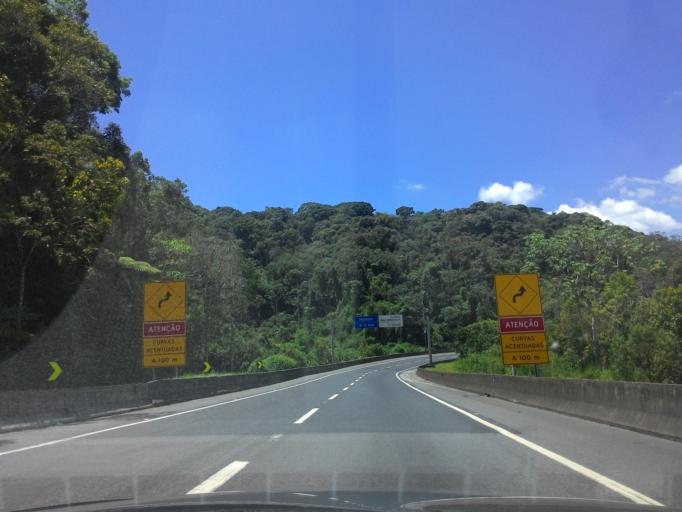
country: BR
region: Sao Paulo
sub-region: Cajati
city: Cajati
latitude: -24.9634
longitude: -48.4302
